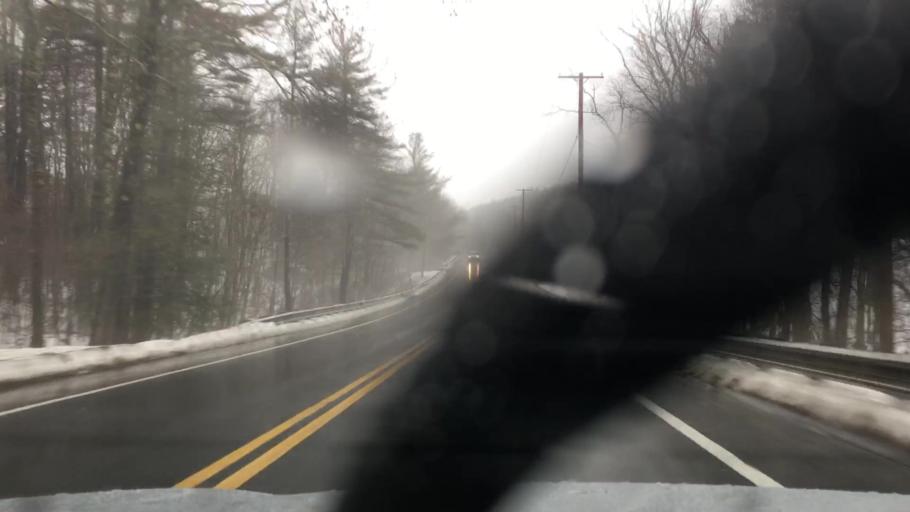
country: US
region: Massachusetts
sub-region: Franklin County
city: Shutesbury
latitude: 42.4892
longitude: -72.3410
